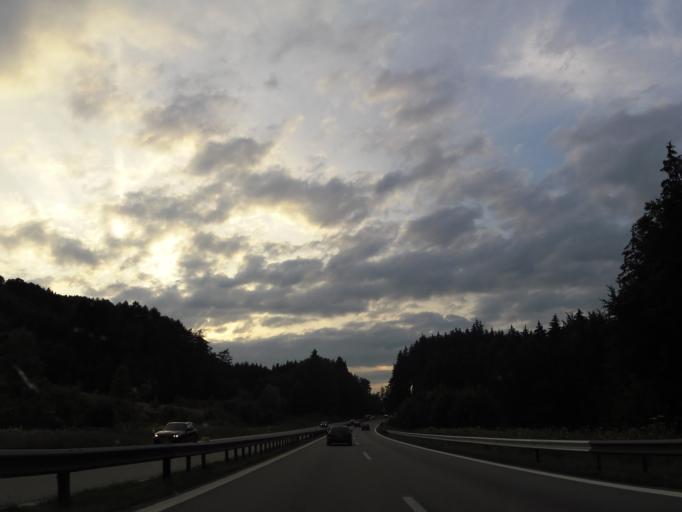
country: DE
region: Bavaria
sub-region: Upper Bavaria
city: Anger
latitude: 47.8103
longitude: 12.8375
